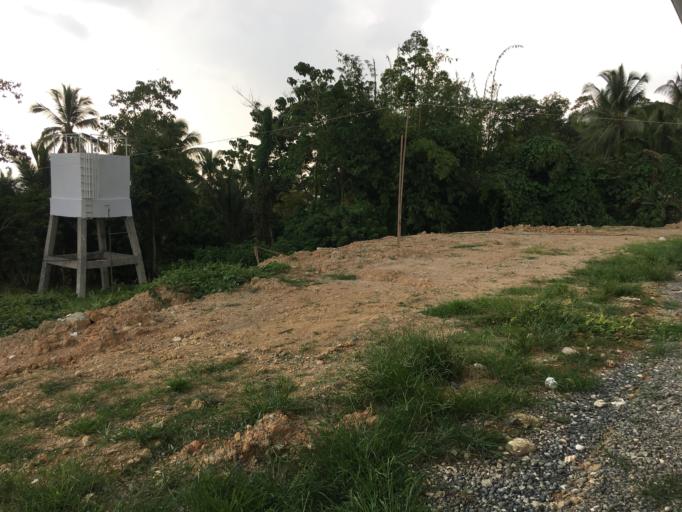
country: PH
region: Davao
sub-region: Province of Davao del Norte
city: New Bohol
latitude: 7.5068
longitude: 125.8874
